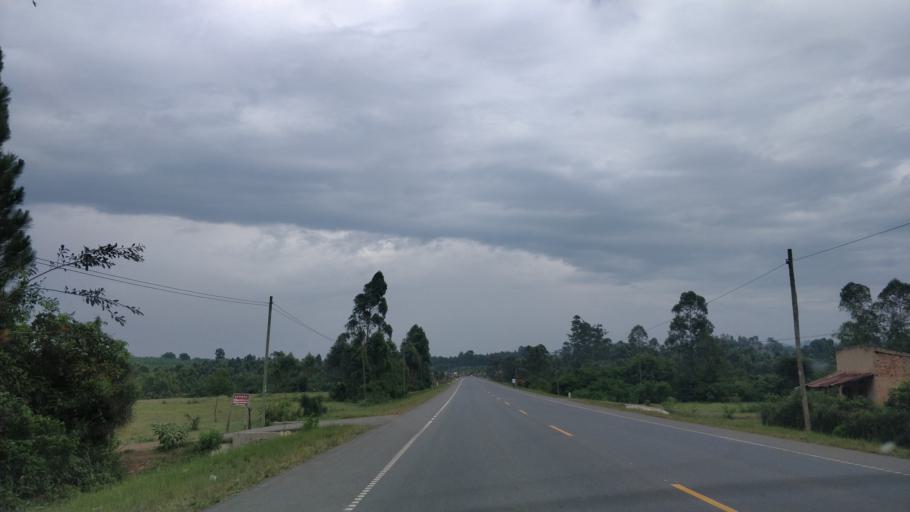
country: UG
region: Western Region
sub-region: Sheema District
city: Kibingo
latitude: -0.6693
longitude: 30.4394
